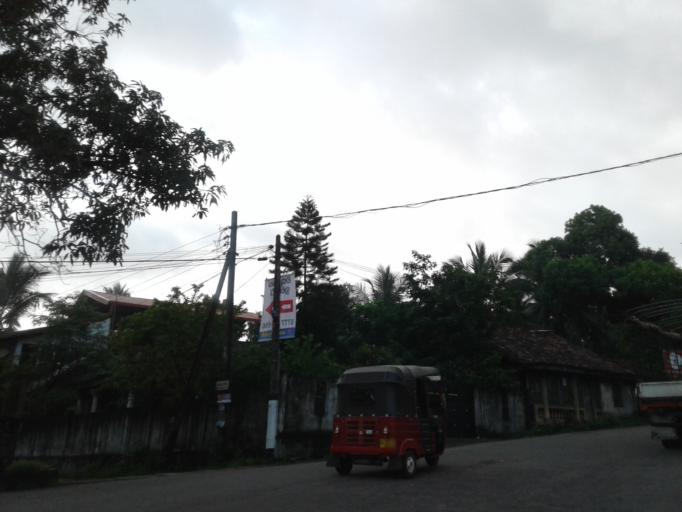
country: LK
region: Western
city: Mulleriyawa
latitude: 6.9289
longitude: 79.9827
